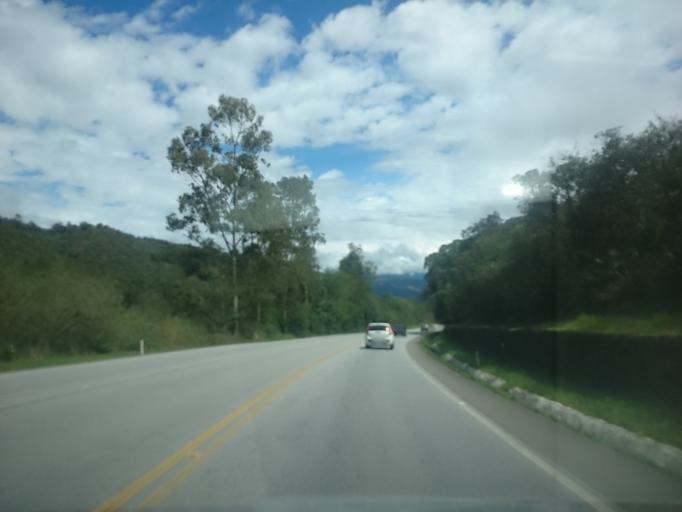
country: BR
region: Santa Catarina
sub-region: Anitapolis
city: Anitapolis
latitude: -27.6697
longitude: -49.2055
